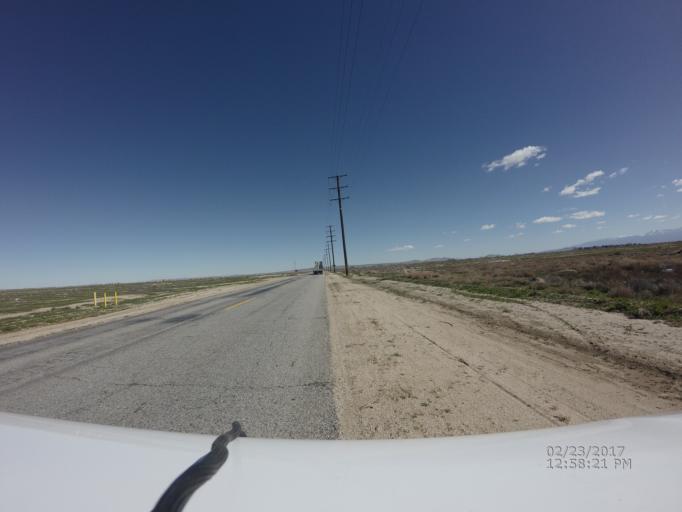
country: US
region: California
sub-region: Los Angeles County
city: Lancaster
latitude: 34.7630
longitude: -118.0443
